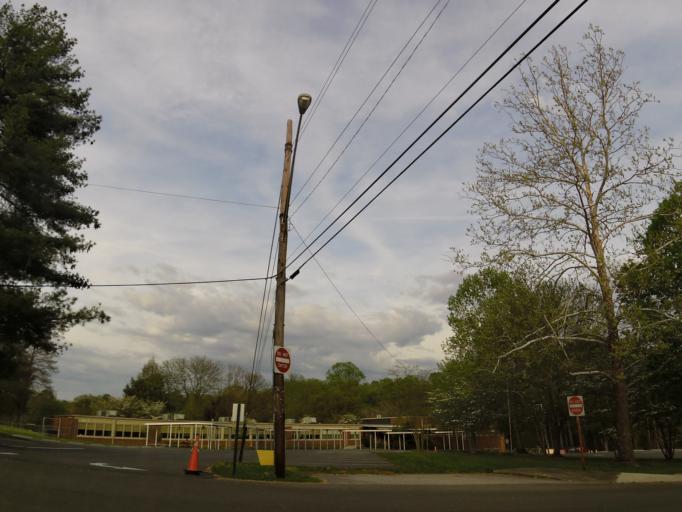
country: US
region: Tennessee
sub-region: Knox County
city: Knoxville
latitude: 36.0514
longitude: -83.9051
